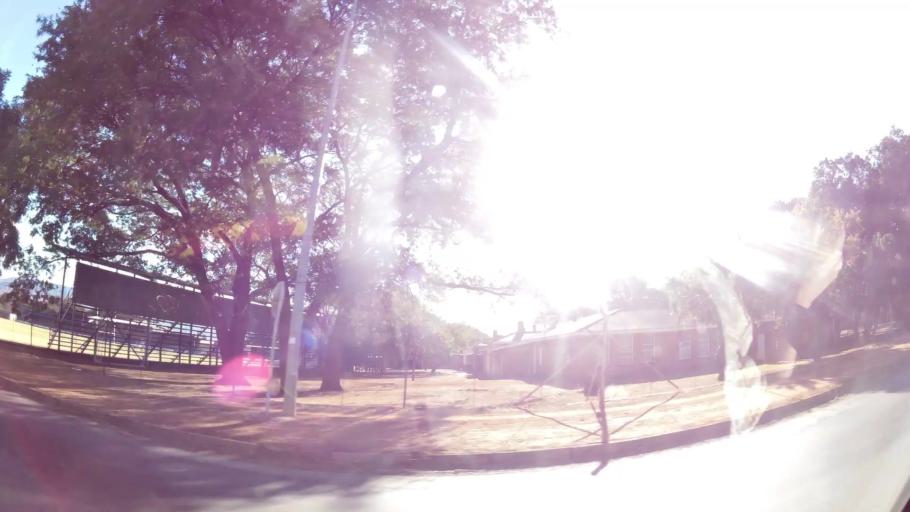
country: ZA
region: Limpopo
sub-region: Waterberg District Municipality
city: Mokopane
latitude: -24.1954
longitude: 29.0085
